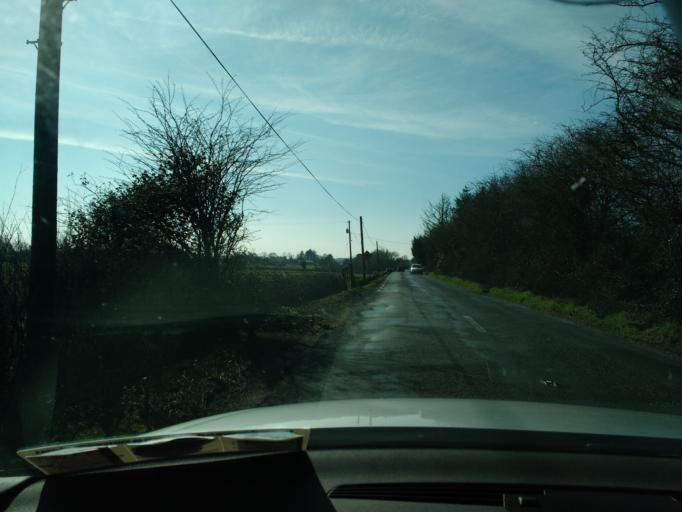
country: IE
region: Munster
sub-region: North Tipperary
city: Newport
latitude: 52.7041
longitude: -8.4540
